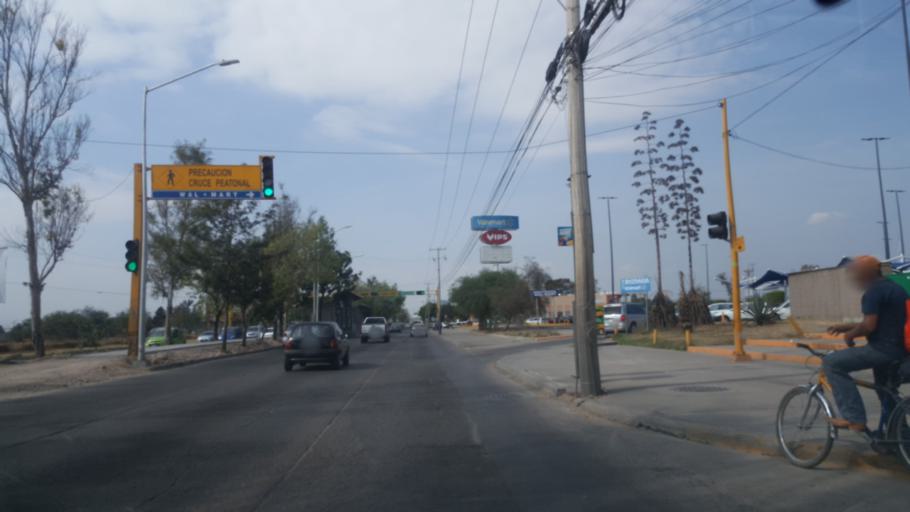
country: MX
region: Guanajuato
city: Leon
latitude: 21.0979
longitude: -101.6607
